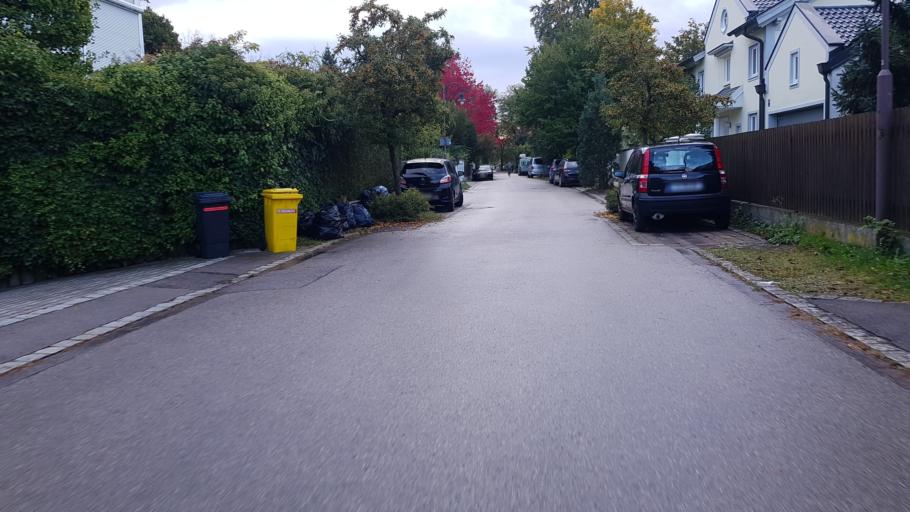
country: DE
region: Bavaria
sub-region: Upper Bavaria
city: Neubiberg
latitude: 48.0764
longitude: 11.6674
